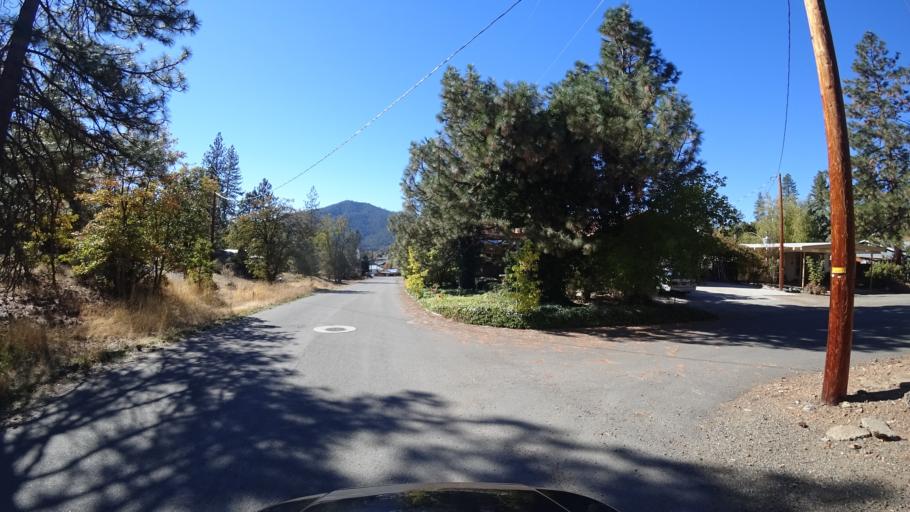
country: US
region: California
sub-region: Siskiyou County
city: Yreka
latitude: 41.6077
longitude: -122.8366
